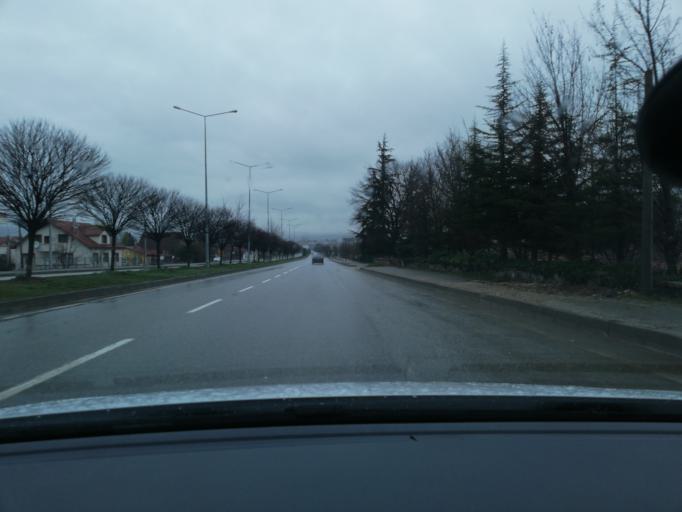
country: TR
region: Bolu
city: Bolu
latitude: 40.7122
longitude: 31.6159
